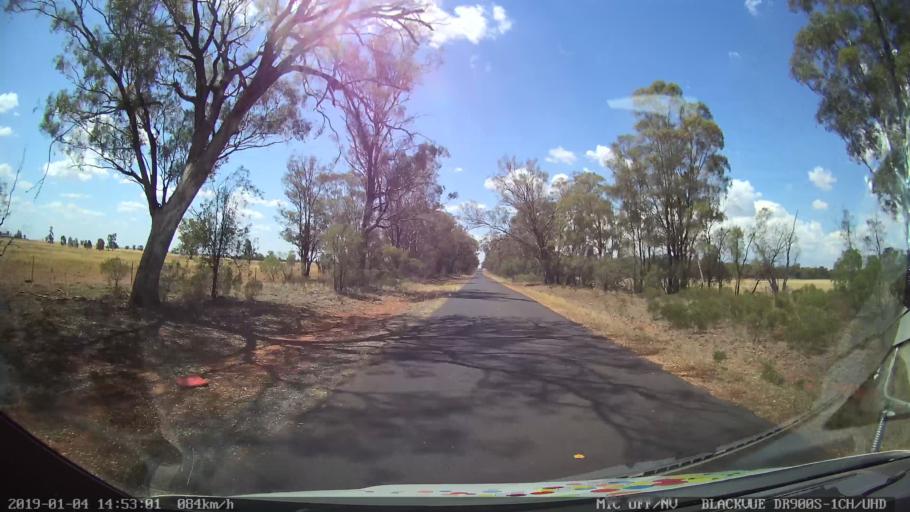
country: AU
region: New South Wales
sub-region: Dubbo Municipality
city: Dubbo
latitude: -32.0083
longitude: 148.6511
